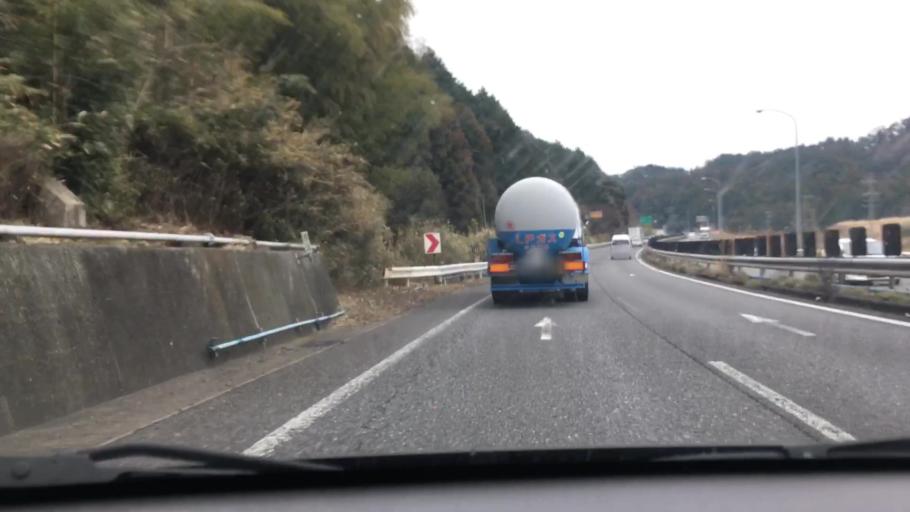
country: JP
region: Mie
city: Kameyama
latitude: 34.8407
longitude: 136.3745
